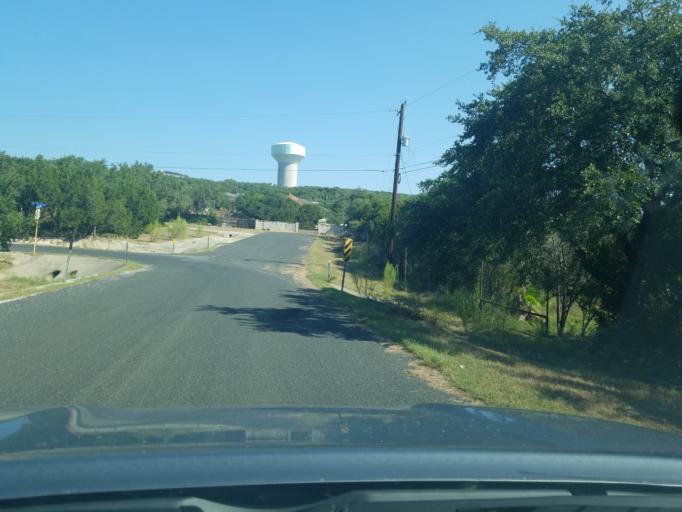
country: US
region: Texas
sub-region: Bexar County
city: Timberwood Park
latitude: 29.6776
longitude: -98.5122
